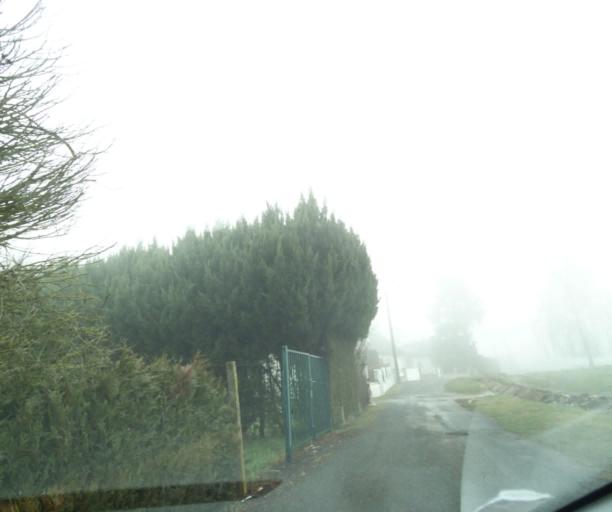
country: FR
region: Ile-de-France
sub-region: Departement de Seine-et-Marne
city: Dammartin-en-Goele
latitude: 49.0502
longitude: 2.6912
